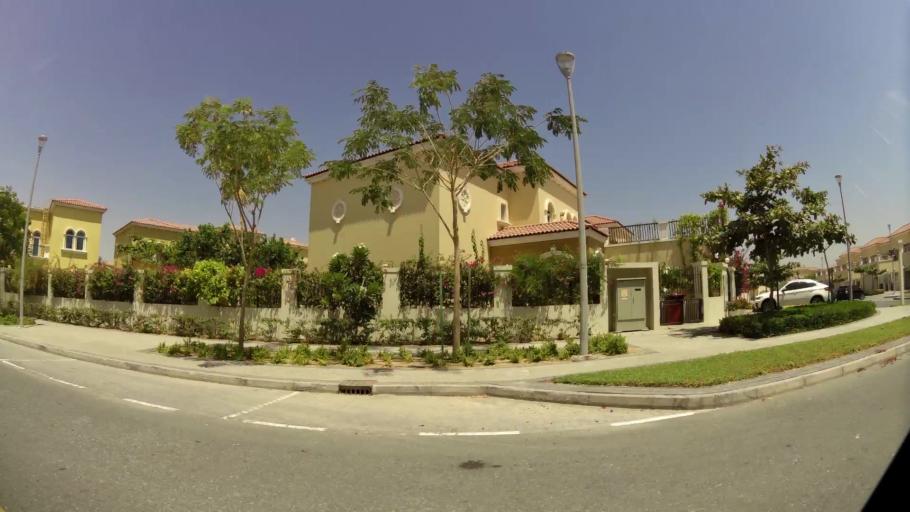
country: AE
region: Dubai
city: Dubai
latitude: 25.0362
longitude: 55.1681
